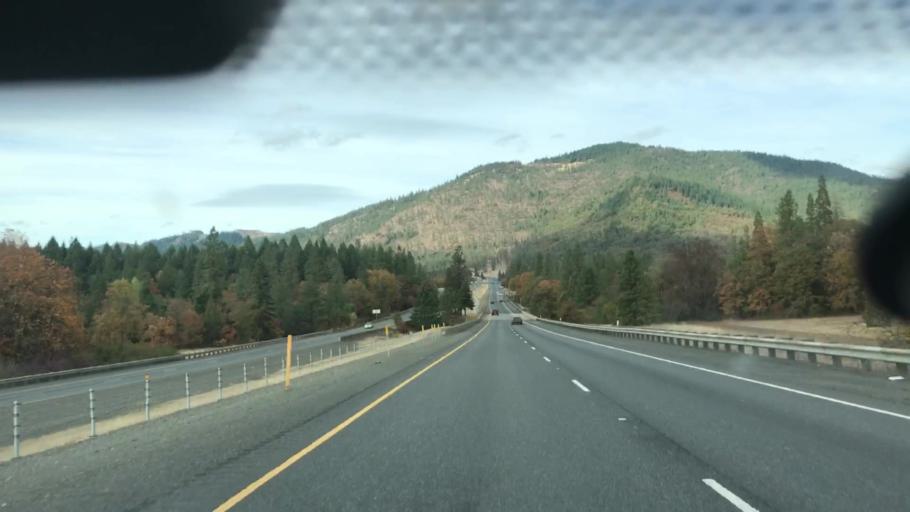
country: US
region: Oregon
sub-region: Josephine County
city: Merlin
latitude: 42.5566
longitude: -123.3713
